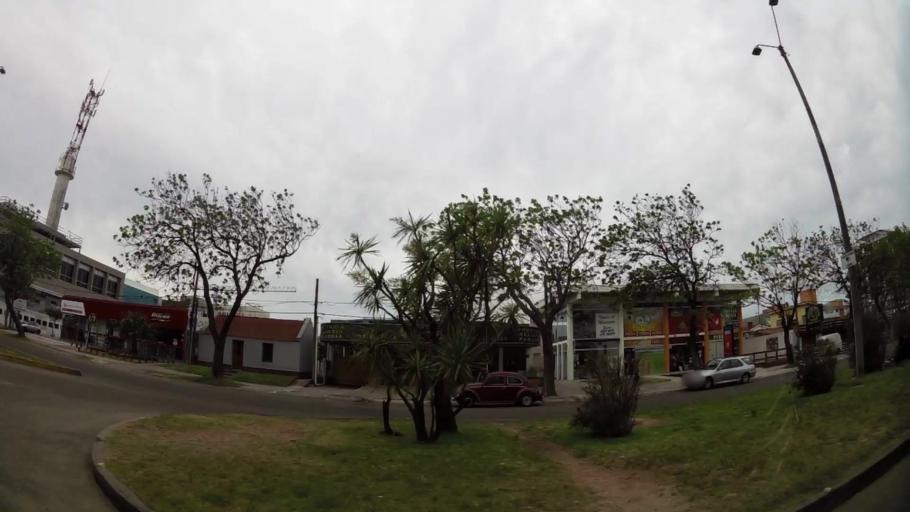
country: UY
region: Maldonado
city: Maldonado
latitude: -34.9089
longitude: -54.9631
